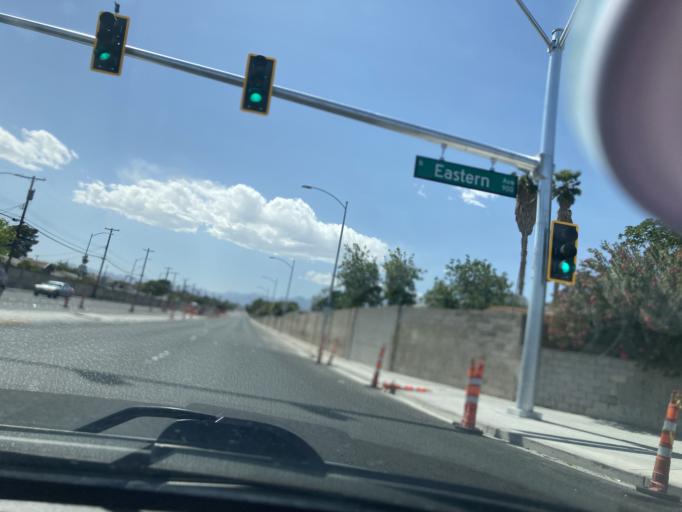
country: US
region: Nevada
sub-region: Clark County
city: North Las Vegas
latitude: 36.1813
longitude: -115.1162
